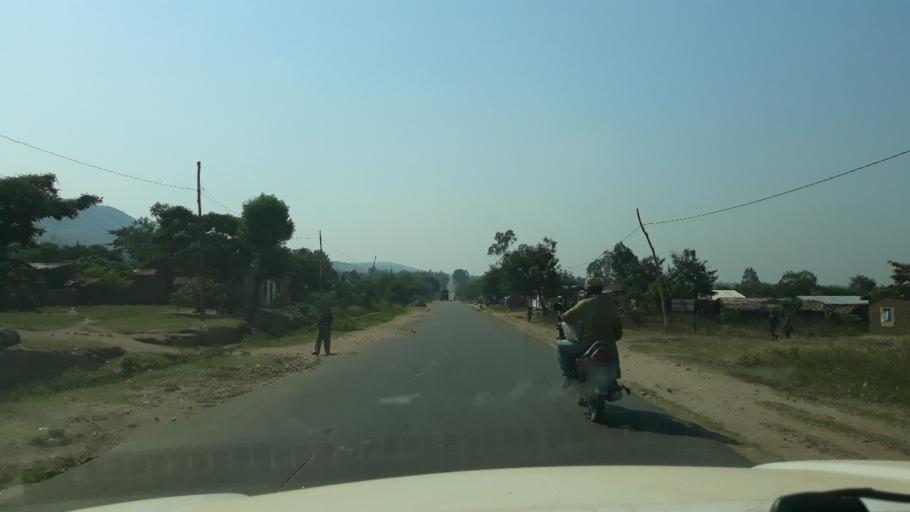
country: CD
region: South Kivu
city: Uvira
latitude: -3.2293
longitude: 29.1661
